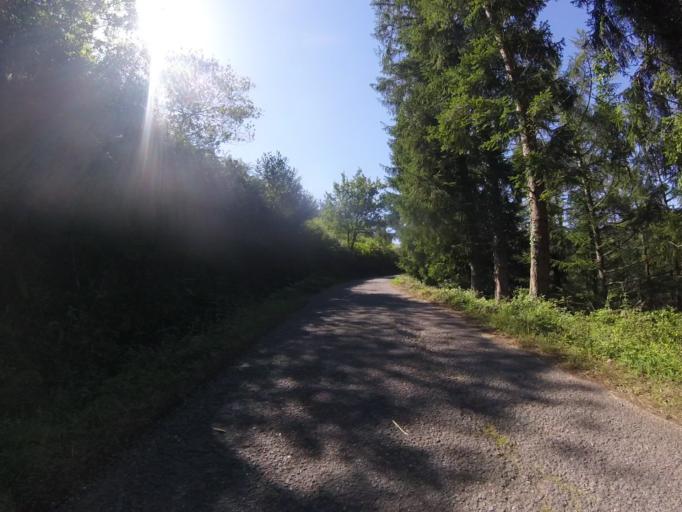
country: ES
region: Navarre
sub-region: Provincia de Navarra
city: Goizueta
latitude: 43.1847
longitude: -1.8278
